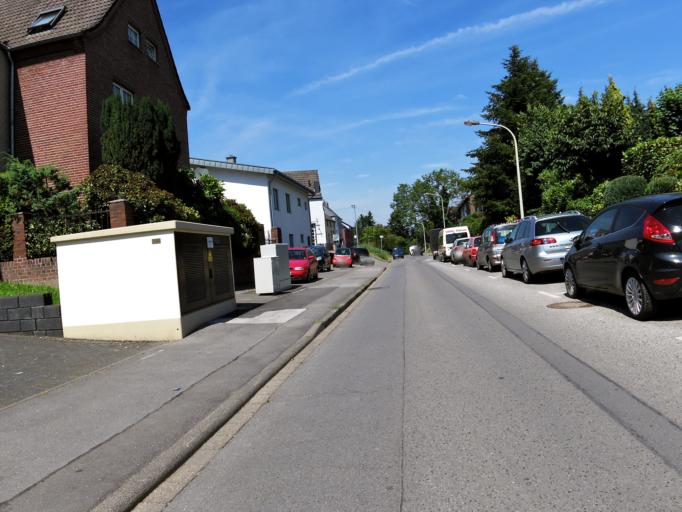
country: NL
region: Limburg
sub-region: Gemeente Kerkrade
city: Kerkrade
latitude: 50.8291
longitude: 6.0697
